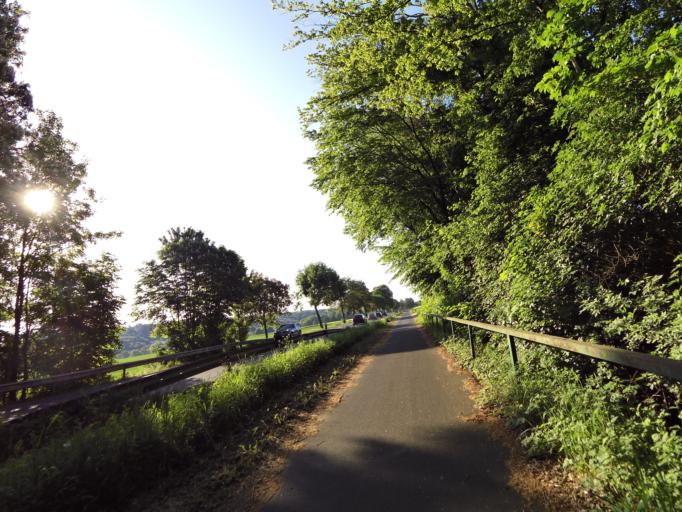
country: DE
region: North Rhine-Westphalia
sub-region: Regierungsbezirk Koln
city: Bonn
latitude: 50.6904
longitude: 7.0722
